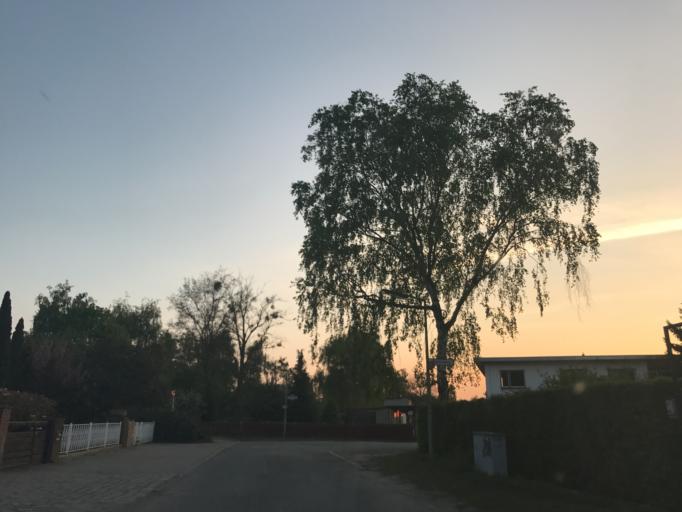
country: DE
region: Berlin
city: Staaken
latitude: 52.5273
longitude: 13.1550
